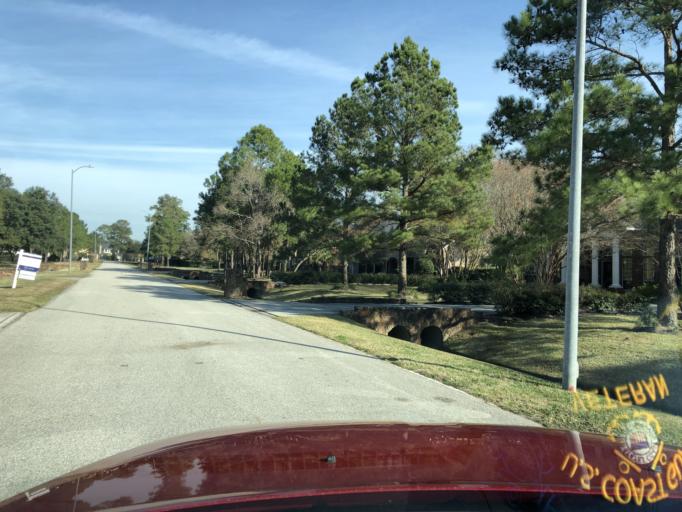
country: US
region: Texas
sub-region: Harris County
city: Tomball
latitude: 30.0374
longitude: -95.5592
